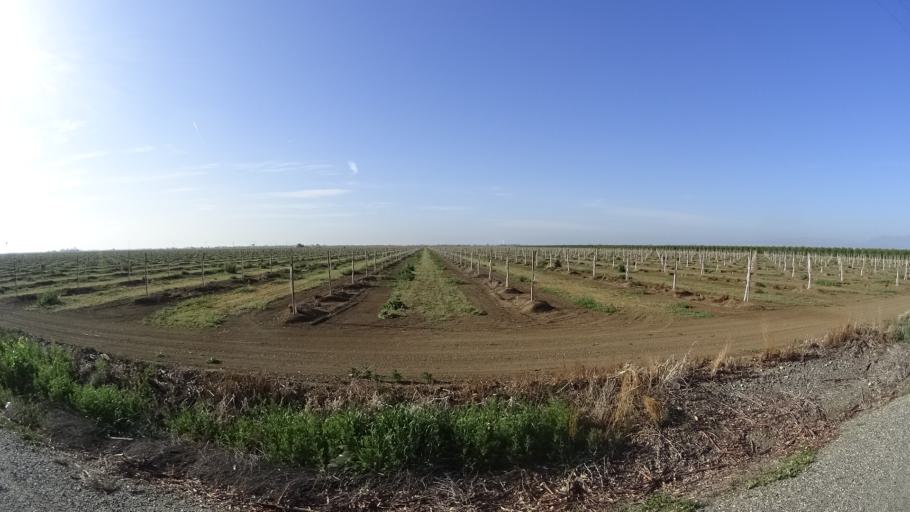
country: US
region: California
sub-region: Glenn County
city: Willows
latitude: 39.5823
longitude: -122.2251
